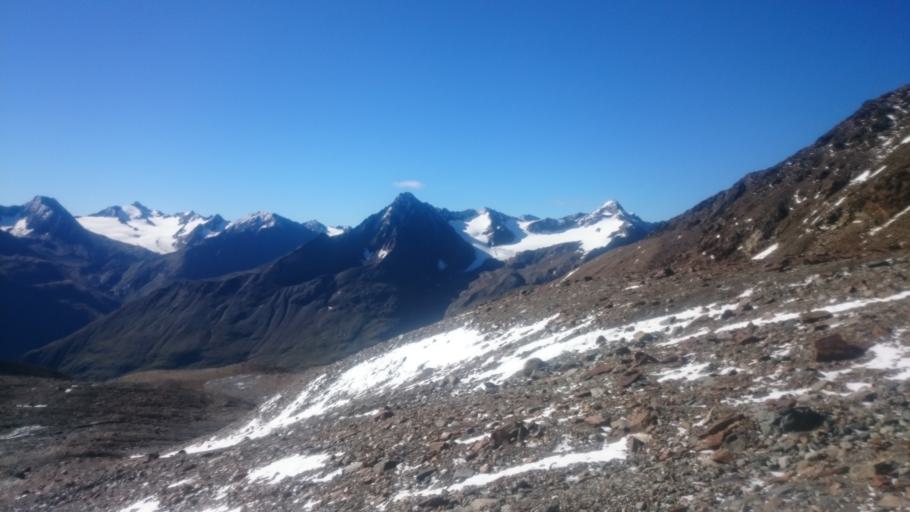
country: AT
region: Tyrol
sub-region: Politischer Bezirk Imst
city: Soelden
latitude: 46.8762
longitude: 10.8611
